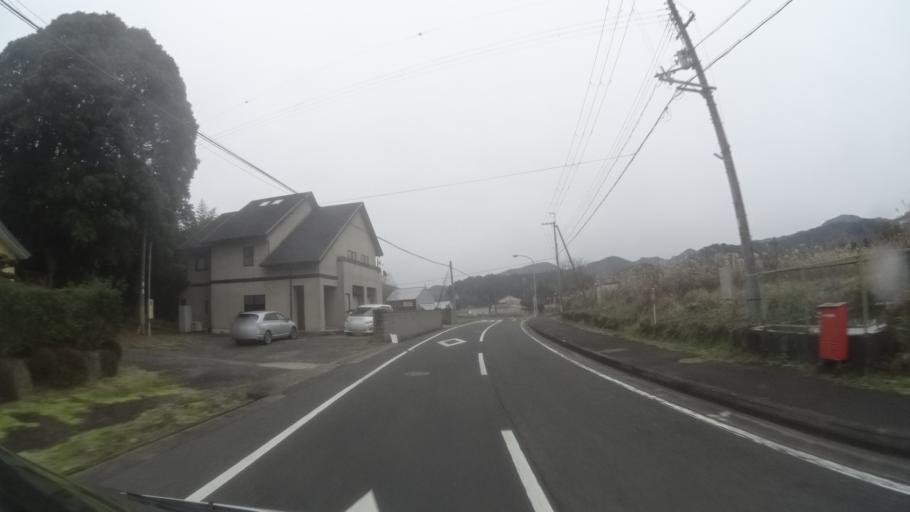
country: JP
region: Kyoto
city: Ayabe
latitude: 35.1738
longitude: 135.3800
